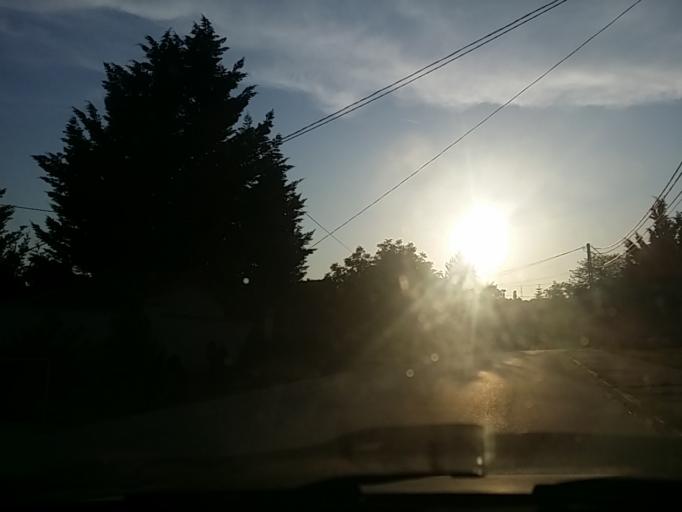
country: HU
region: Pest
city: Urom
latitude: 47.5803
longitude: 19.0316
